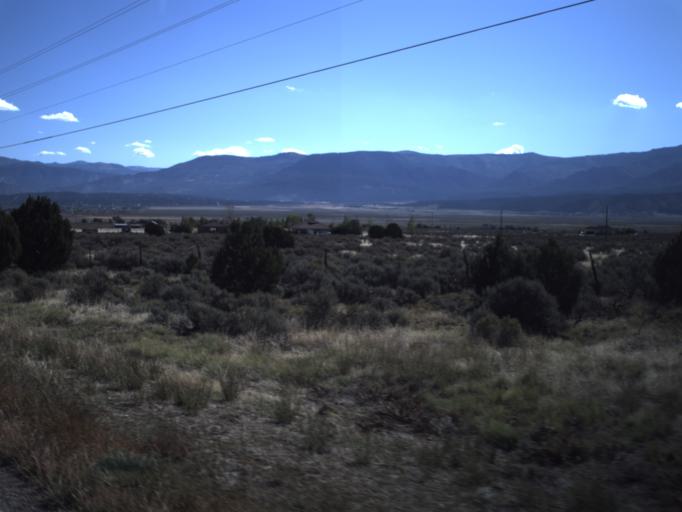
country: US
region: Utah
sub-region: Iron County
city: Cedar City
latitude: 37.6457
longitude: -113.2433
